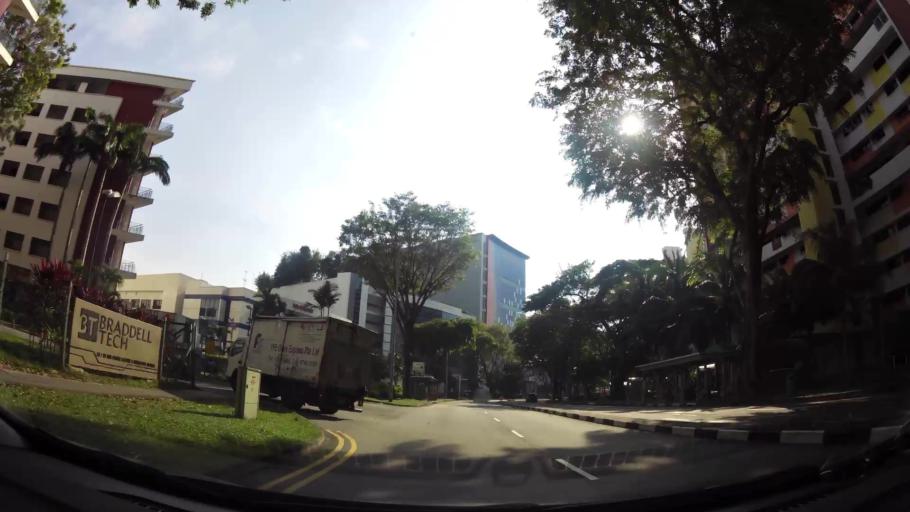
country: SG
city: Singapore
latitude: 1.3399
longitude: 103.8579
